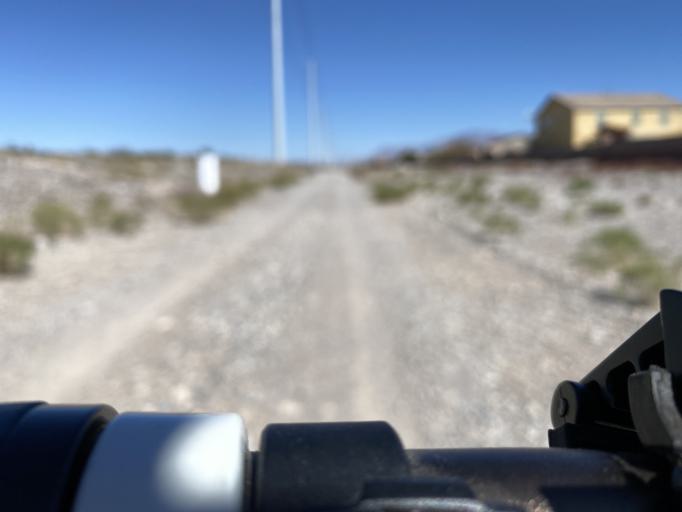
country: US
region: Nevada
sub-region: Clark County
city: Summerlin South
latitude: 36.2950
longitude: -115.3335
